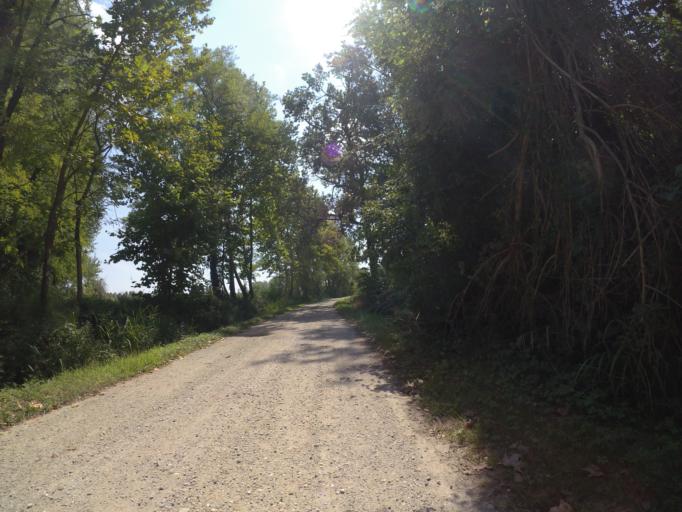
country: IT
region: Friuli Venezia Giulia
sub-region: Provincia di Udine
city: Bertiolo
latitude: 45.9132
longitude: 13.0610
